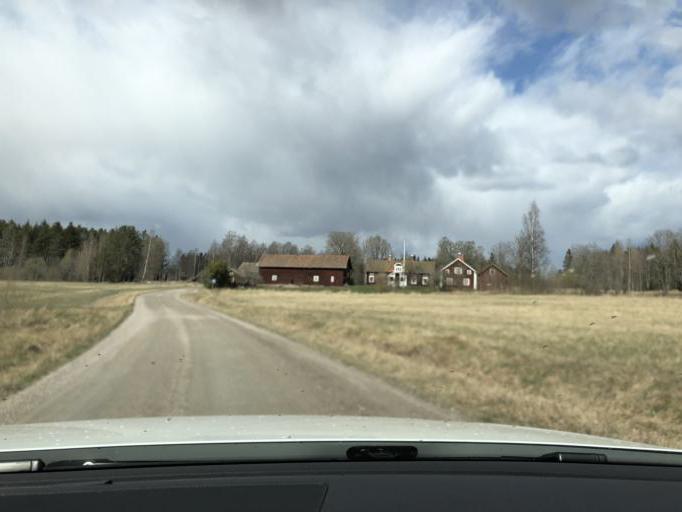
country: SE
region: Gaevleborg
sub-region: Gavle Kommun
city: Hedesunda
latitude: 60.3106
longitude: 17.1101
